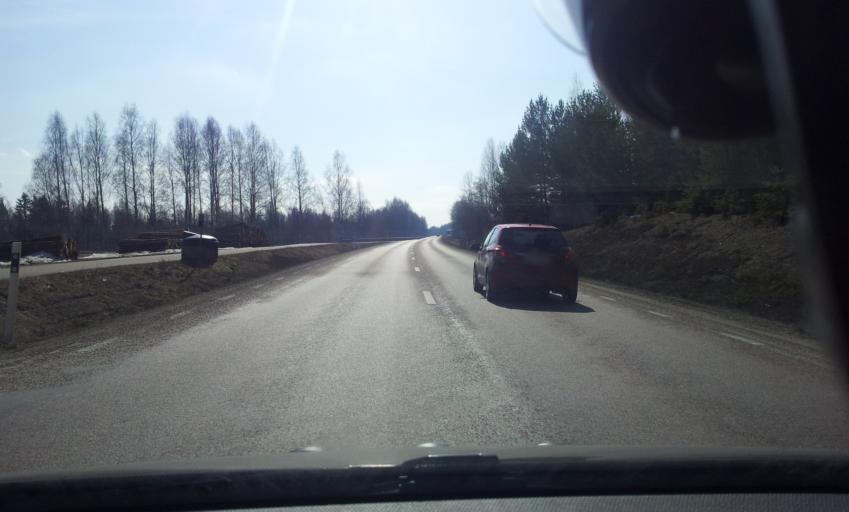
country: SE
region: Gaevleborg
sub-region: Ljusdals Kommun
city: Jaervsoe
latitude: 61.7632
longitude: 16.1591
